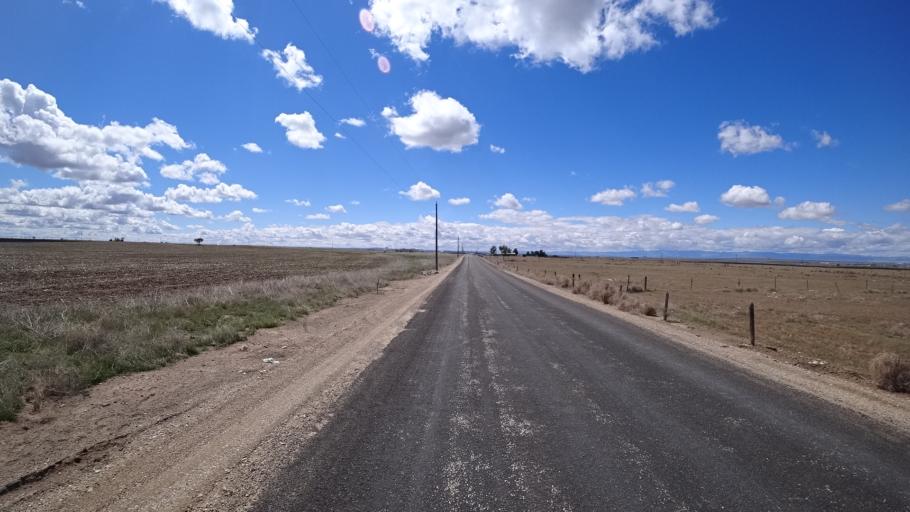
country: US
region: Idaho
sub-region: Ada County
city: Kuna
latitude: 43.4629
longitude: -116.2744
